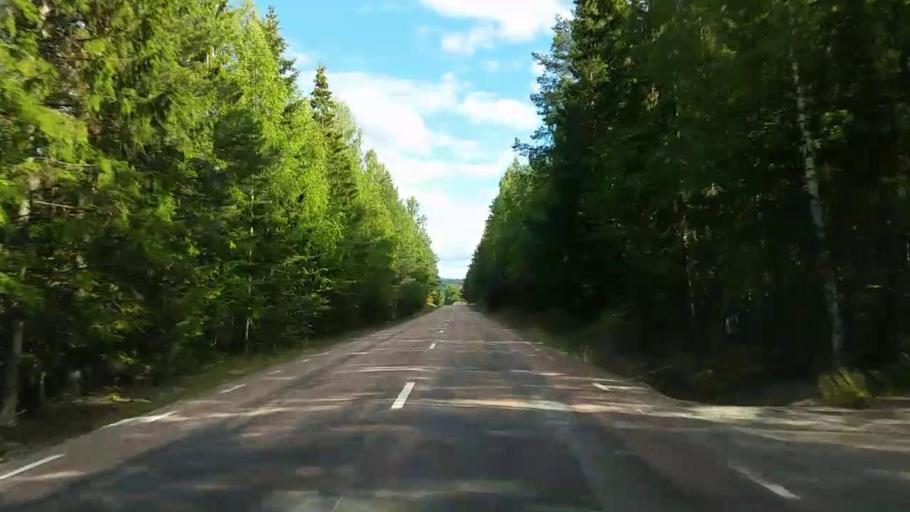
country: SE
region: Gaevleborg
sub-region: Ljusdals Kommun
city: Farila
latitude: 61.9129
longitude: 15.8842
